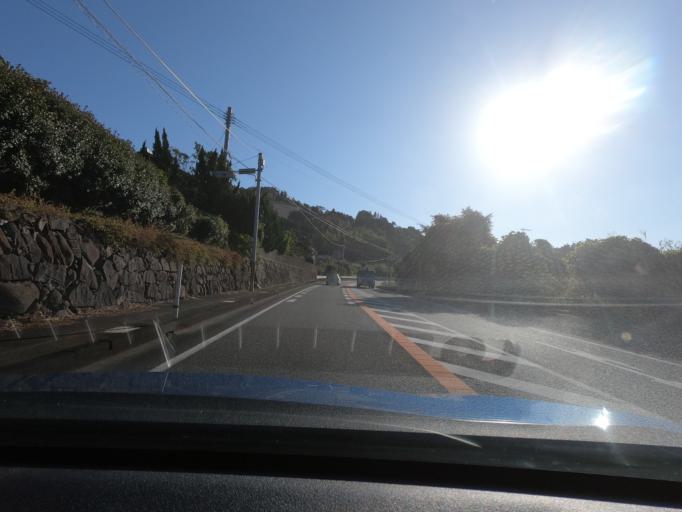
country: JP
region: Kagoshima
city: Izumi
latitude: 32.1506
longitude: 130.3639
